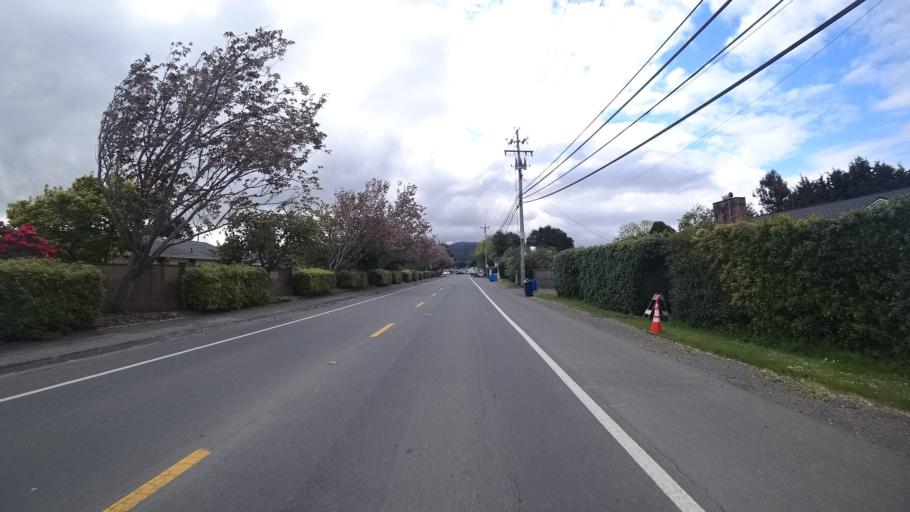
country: US
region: California
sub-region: Humboldt County
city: Arcata
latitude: 40.8910
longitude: -124.0894
